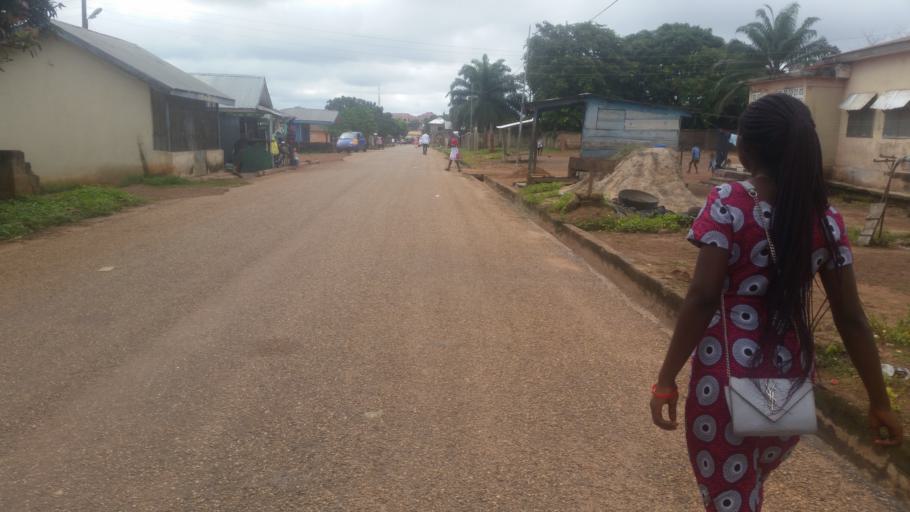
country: GH
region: Brong-Ahafo
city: Sunyani
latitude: 7.3462
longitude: -2.3245
